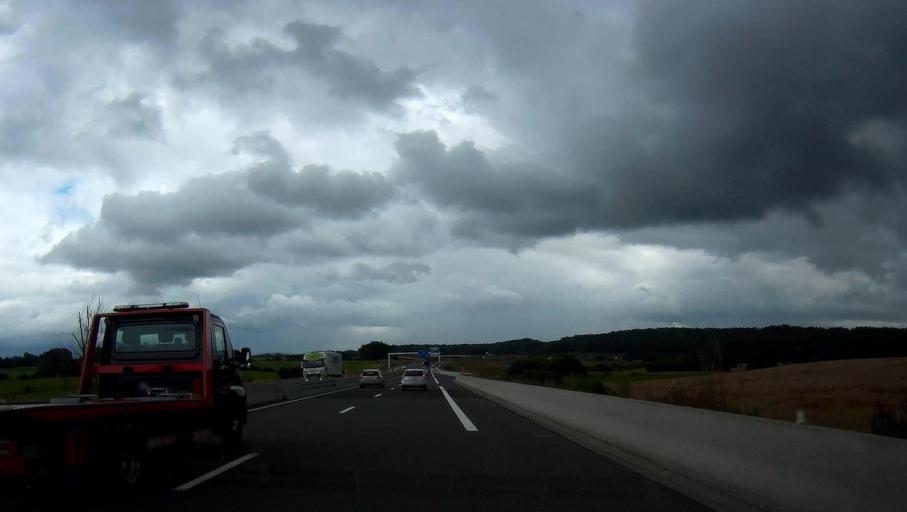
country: FR
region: Champagne-Ardenne
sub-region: Departement des Ardennes
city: Tournes
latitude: 49.7691
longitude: 4.6329
